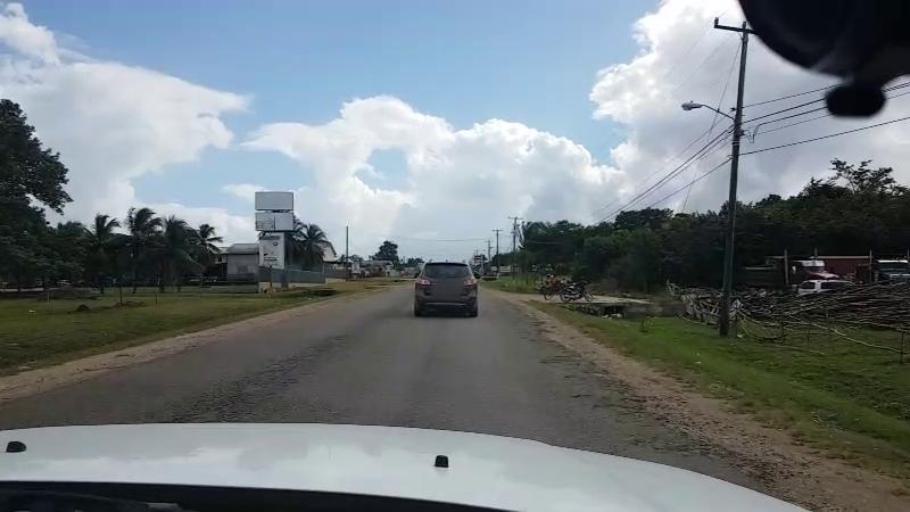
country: BZ
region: Cayo
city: Belmopan
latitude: 17.2483
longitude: -88.7843
